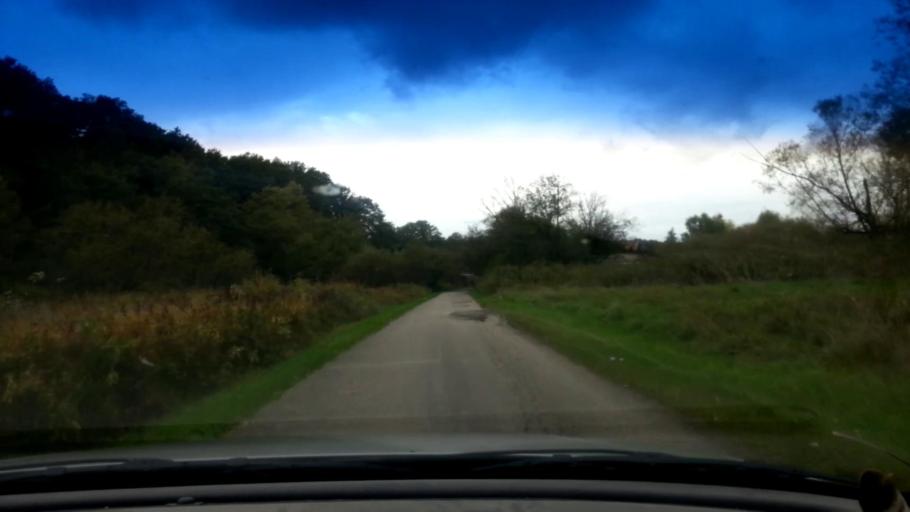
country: DE
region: Bavaria
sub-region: Upper Franconia
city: Priesendorf
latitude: 49.8948
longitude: 10.7175
